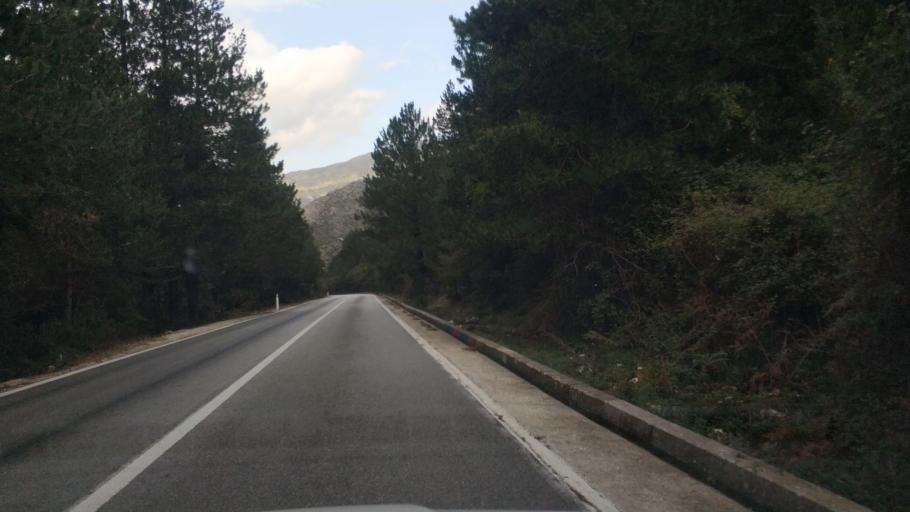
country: AL
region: Vlore
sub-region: Rrethi i Vlores
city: Brataj
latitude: 40.2260
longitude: 19.5782
